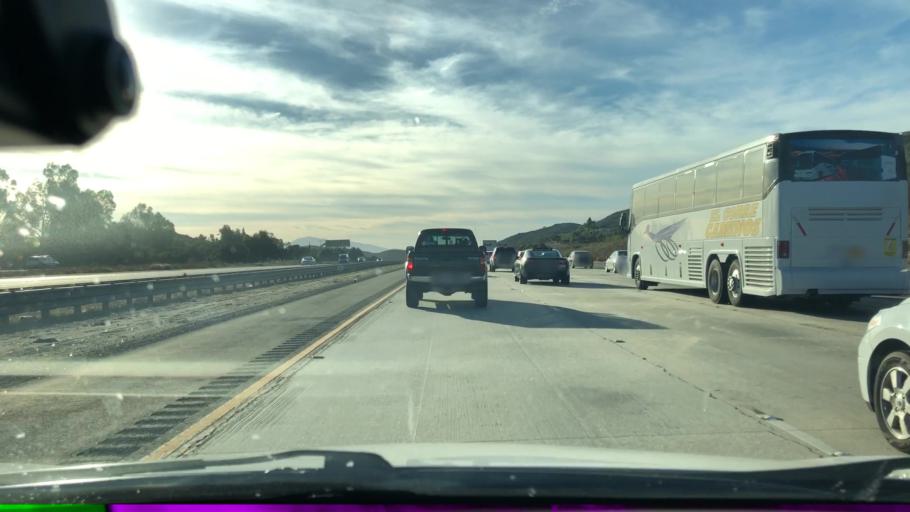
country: US
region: California
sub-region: San Diego County
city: Hidden Meadows
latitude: 33.1875
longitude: -117.1202
